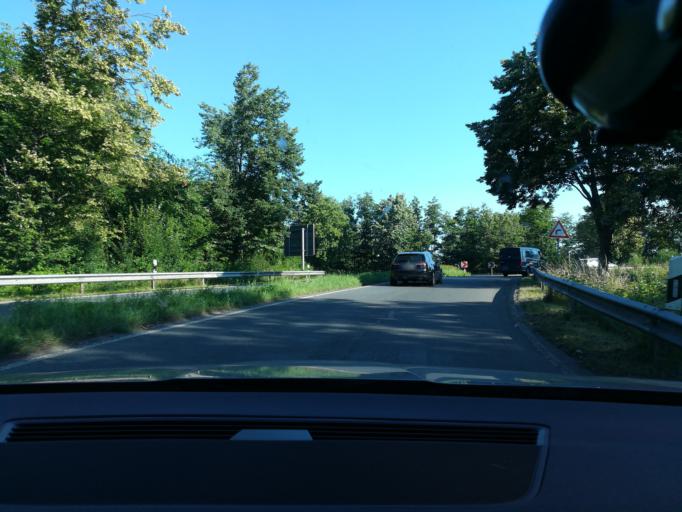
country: DE
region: North Rhine-Westphalia
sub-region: Regierungsbezirk Detmold
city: Minden
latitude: 52.2635
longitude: 8.8963
